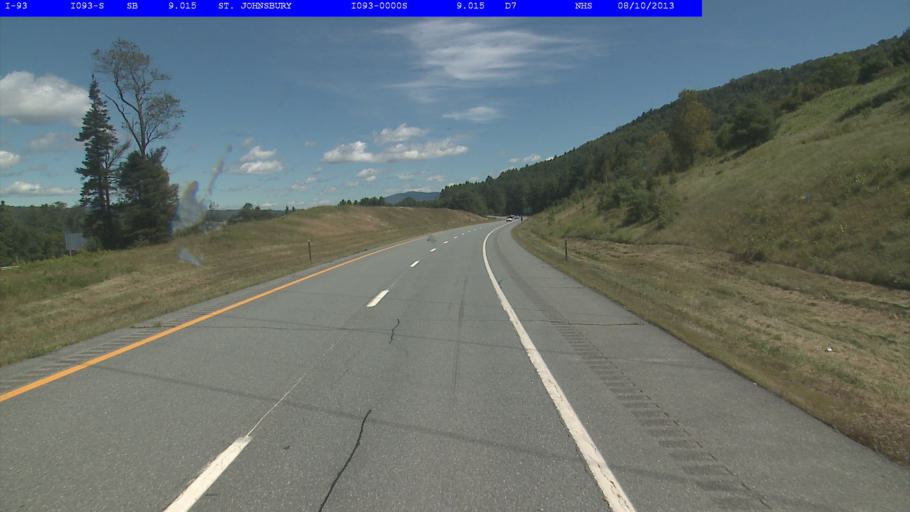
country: US
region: Vermont
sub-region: Caledonia County
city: Saint Johnsbury
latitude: 44.4154
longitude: -71.9823
